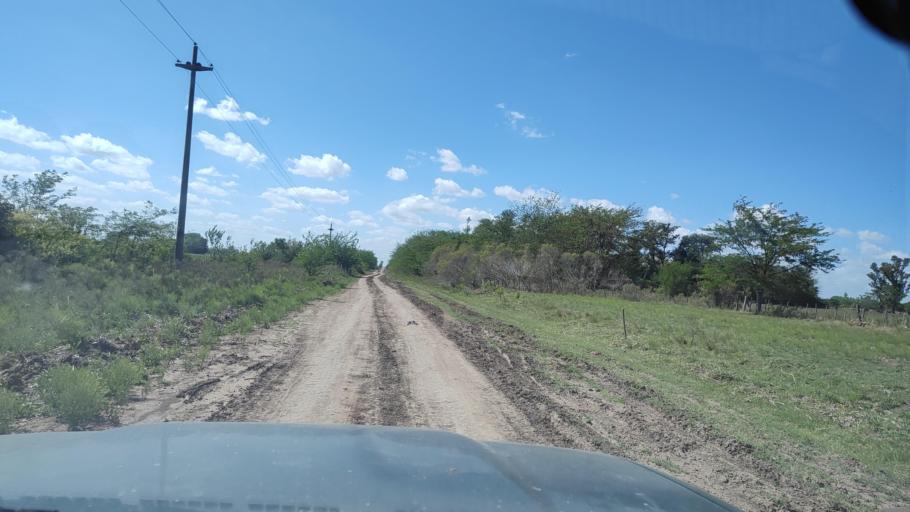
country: AR
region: Buenos Aires
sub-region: Partido de Lujan
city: Lujan
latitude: -34.5284
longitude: -59.1527
